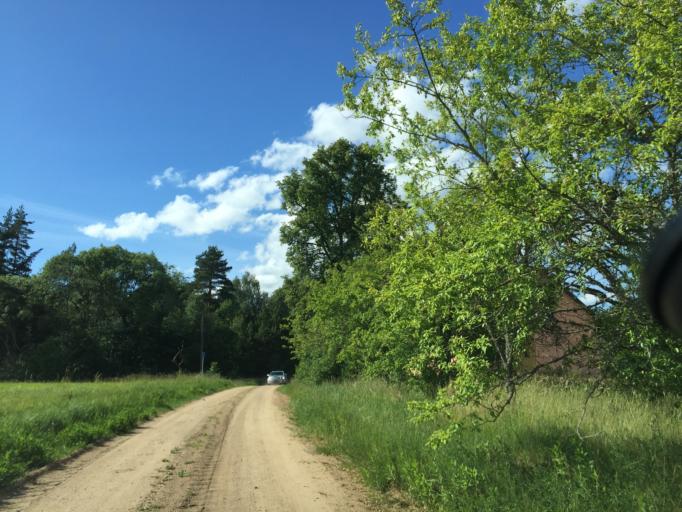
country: LV
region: Vecumnieki
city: Vecumnieki
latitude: 56.4347
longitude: 24.5947
